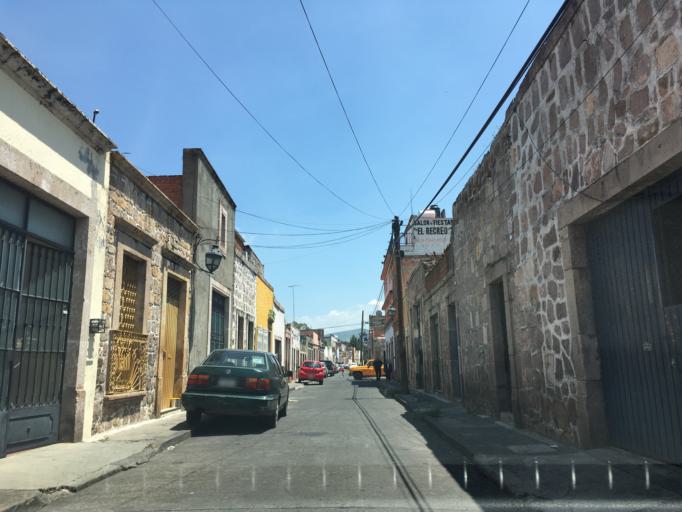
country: MX
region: Michoacan
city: Morelia
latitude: 19.7070
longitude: -101.1861
